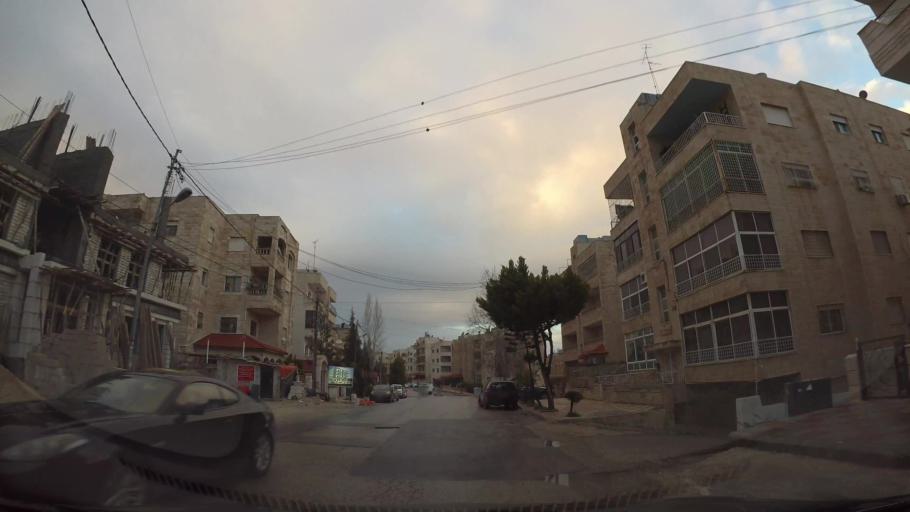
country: JO
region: Amman
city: Amman
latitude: 31.9874
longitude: 35.9157
